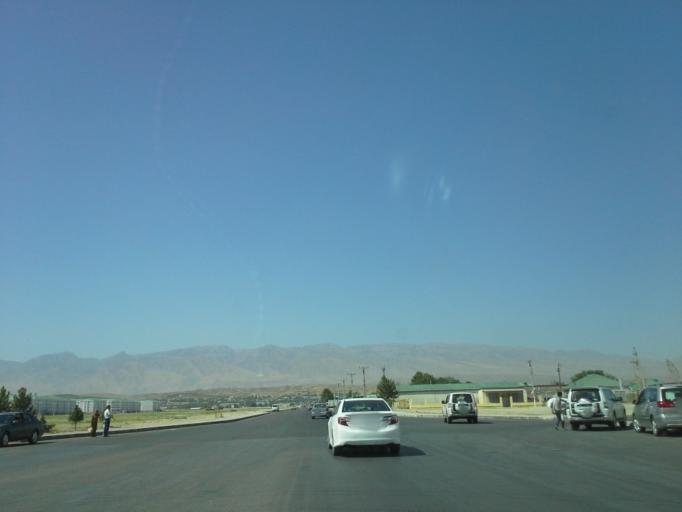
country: TM
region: Ahal
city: Ashgabat
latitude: 37.9858
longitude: 58.3267
